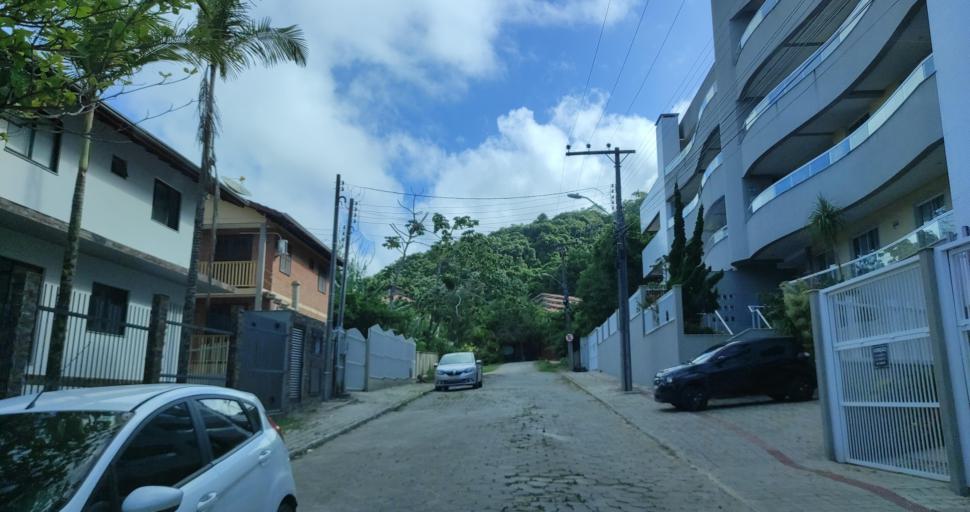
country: BR
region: Santa Catarina
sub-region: Porto Belo
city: Porto Belo
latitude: -27.1523
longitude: -48.4917
